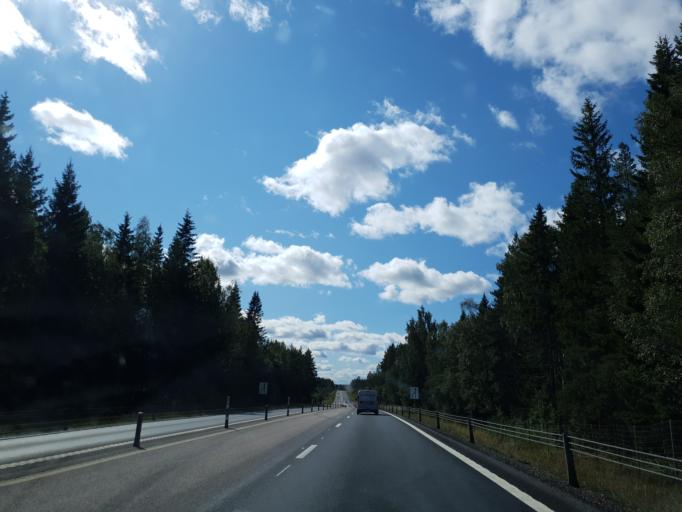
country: SE
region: Vaesterbotten
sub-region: Nordmalings Kommun
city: Nordmaling
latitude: 63.5140
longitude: 19.3620
